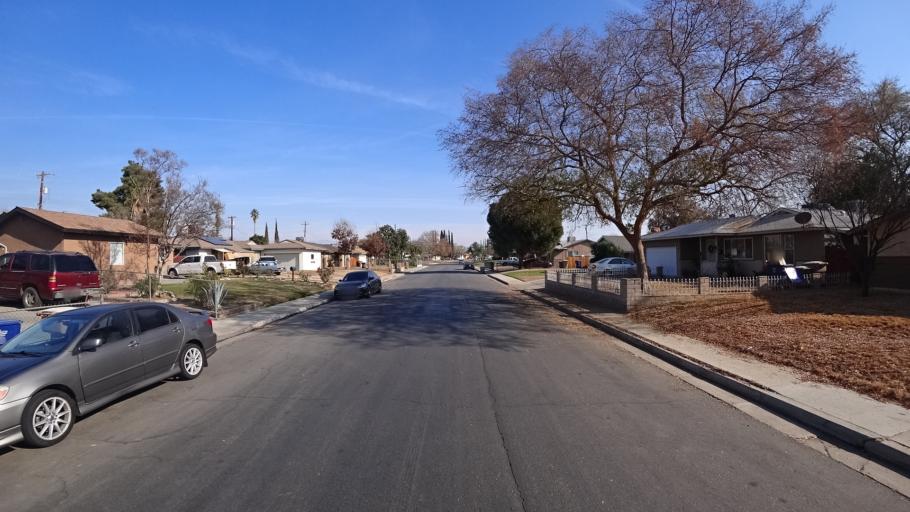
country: US
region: California
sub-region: Kern County
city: Bakersfield
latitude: 35.3289
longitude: -119.0189
